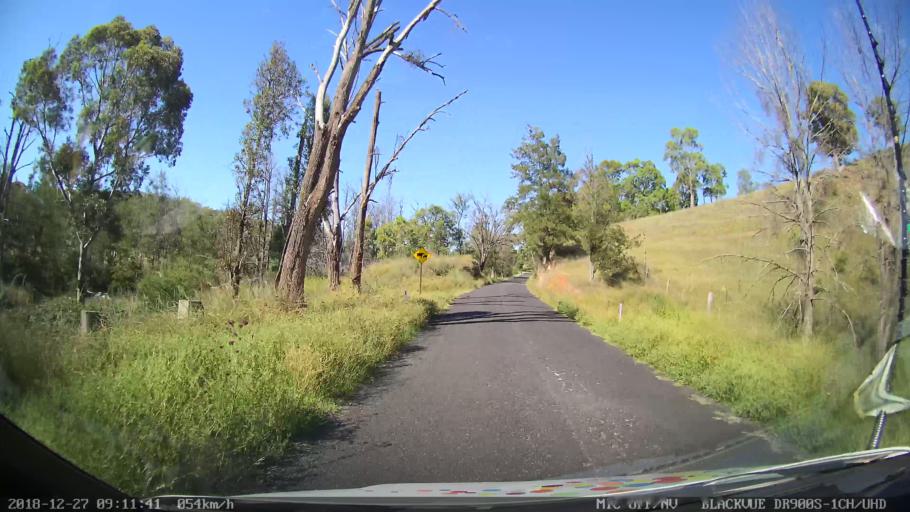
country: AU
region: New South Wales
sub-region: Lithgow
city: Portland
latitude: -33.1371
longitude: 150.1123
